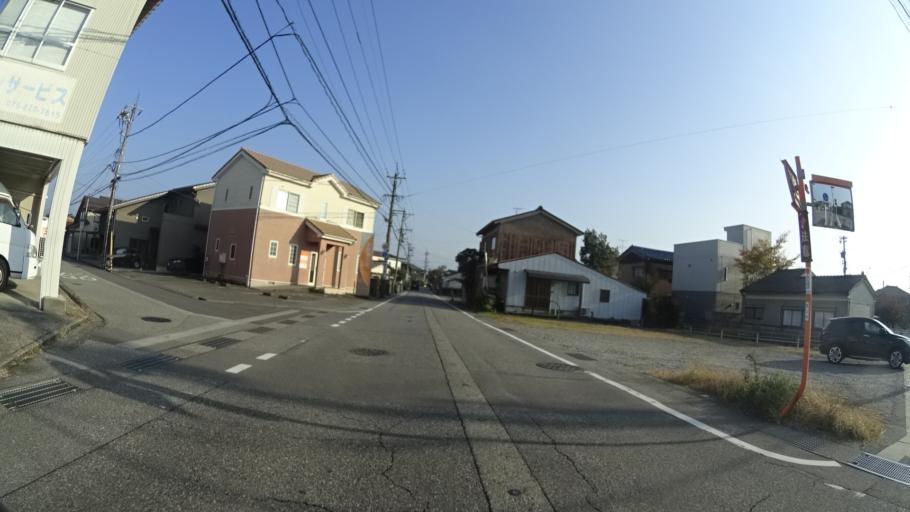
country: JP
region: Toyama
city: Toyama-shi
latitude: 36.6955
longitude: 137.2673
